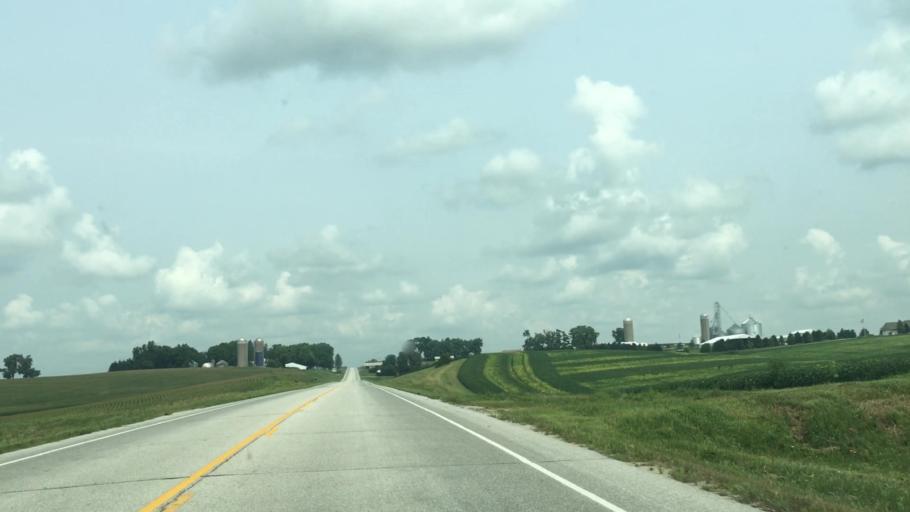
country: US
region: Minnesota
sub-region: Fillmore County
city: Harmony
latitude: 43.6092
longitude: -91.9297
